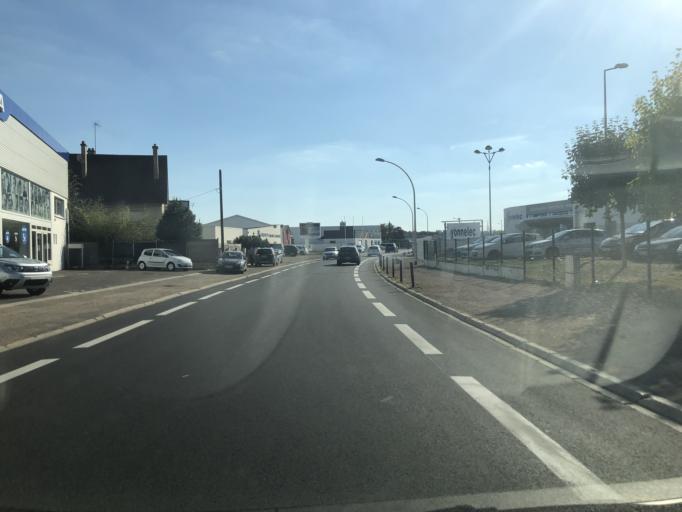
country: FR
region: Bourgogne
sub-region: Departement de l'Yonne
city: Auxerre
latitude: 47.8121
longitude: 3.5850
